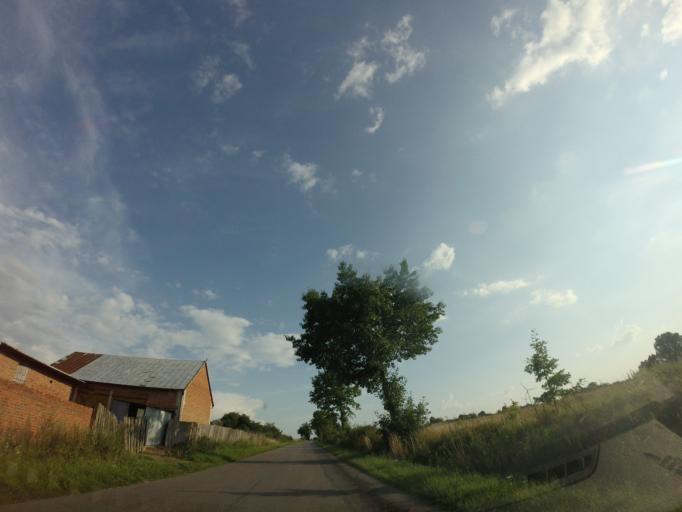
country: PL
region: Lublin Voivodeship
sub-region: Powiat lubartowski
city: Michow
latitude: 51.5171
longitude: 22.3110
